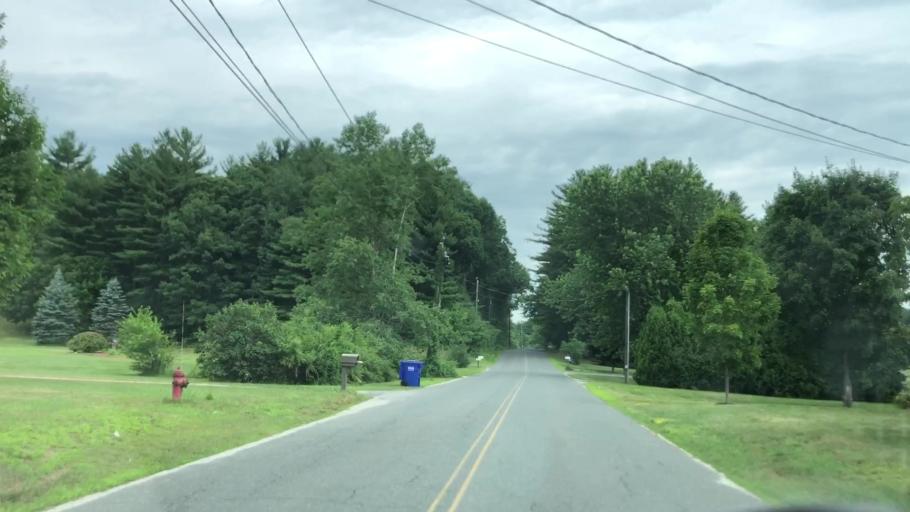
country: US
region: Massachusetts
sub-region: Hampshire County
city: Southampton
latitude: 42.2157
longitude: -72.6806
